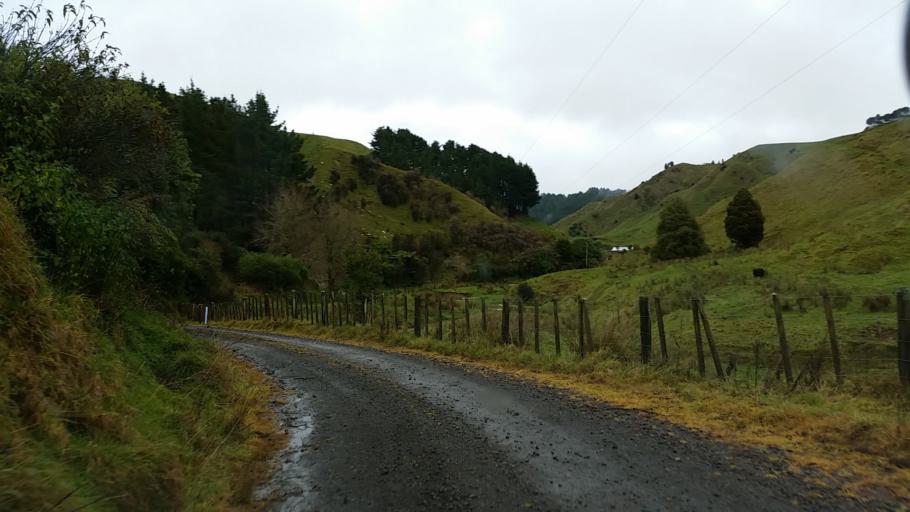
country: NZ
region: Taranaki
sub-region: South Taranaki District
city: Eltham
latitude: -39.4875
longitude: 174.4346
